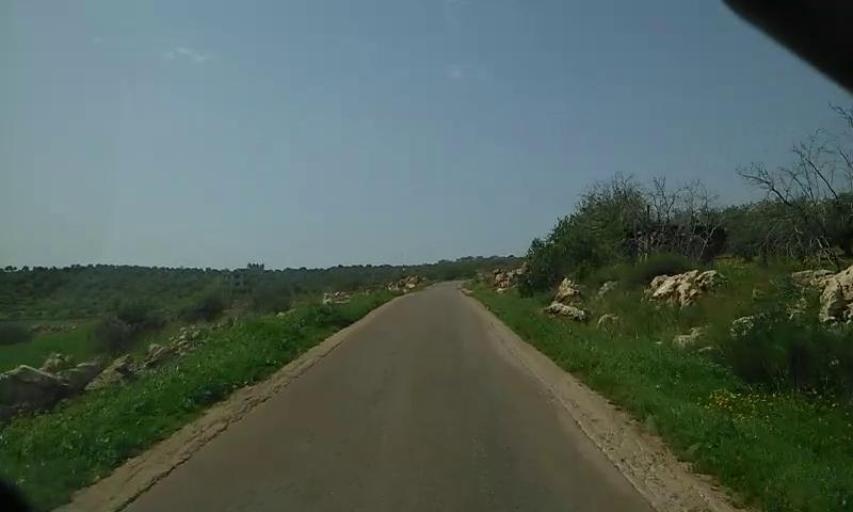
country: PS
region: West Bank
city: At Taybah
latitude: 32.4981
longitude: 35.1910
